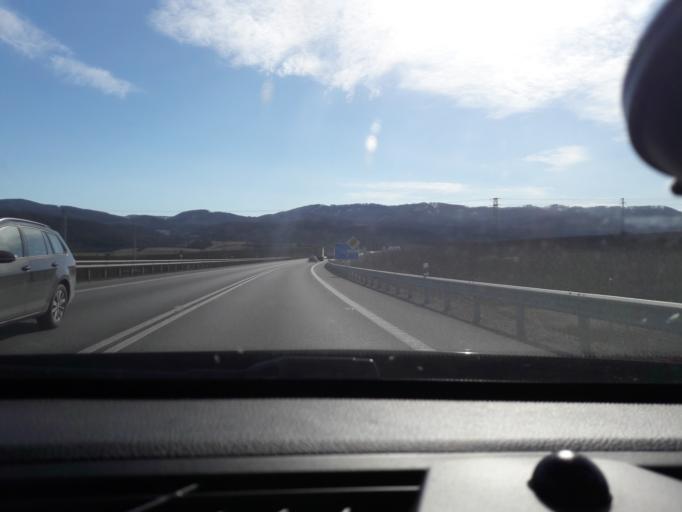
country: SK
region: Banskobystricky
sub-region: Okres Banska Bystrica
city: Zvolen
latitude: 48.5704
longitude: 19.2412
